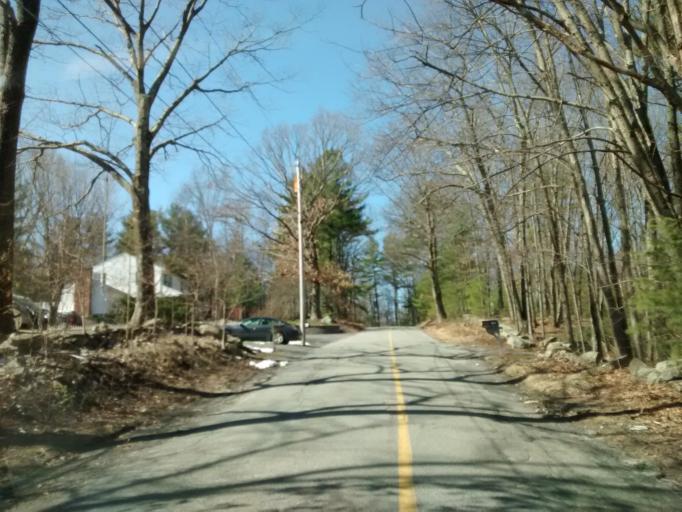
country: US
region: Massachusetts
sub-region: Worcester County
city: Northbridge
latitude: 42.1610
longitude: -71.6885
